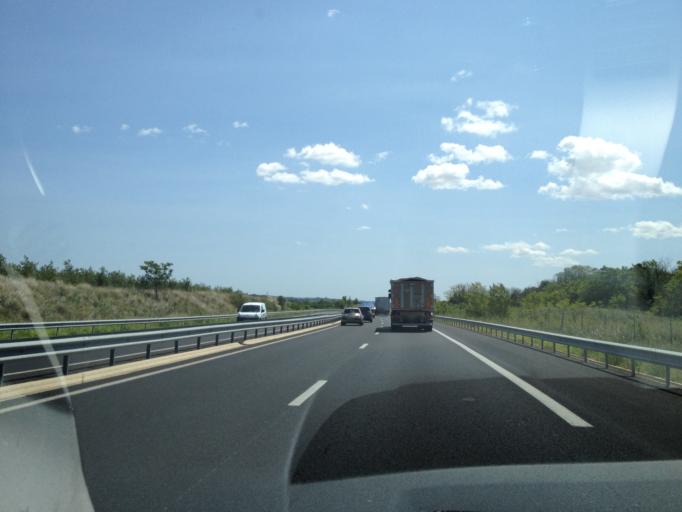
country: FR
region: Languedoc-Roussillon
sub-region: Departement de l'Herault
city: Nebian
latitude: 43.6007
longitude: 3.4615
